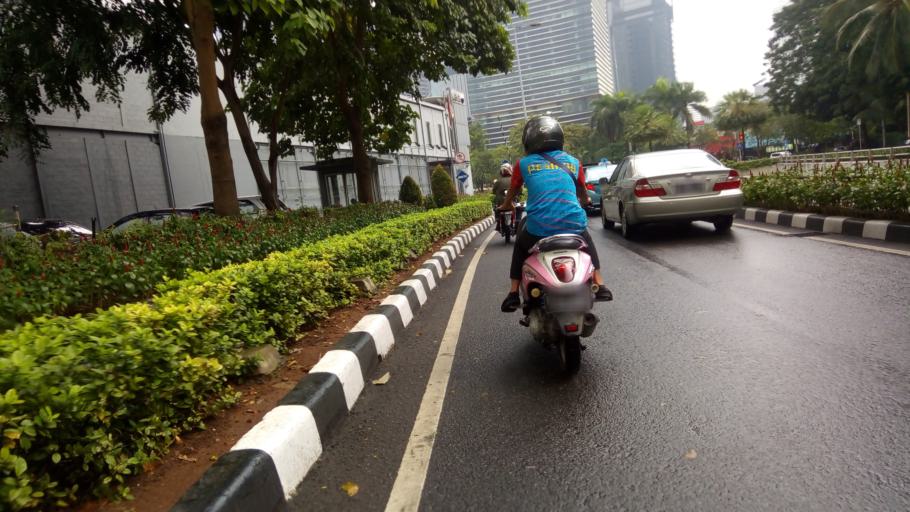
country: ID
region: Jakarta Raya
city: Jakarta
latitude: -6.2271
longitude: 106.8116
